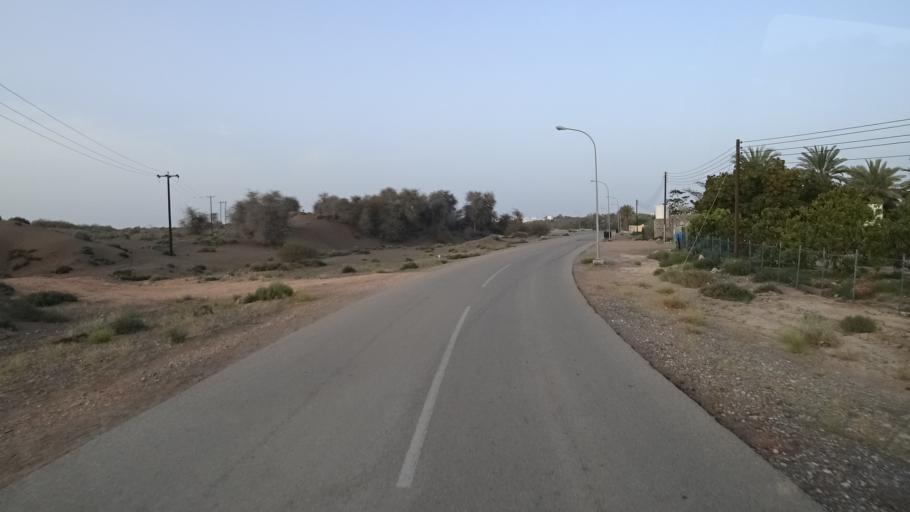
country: OM
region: Muhafazat Masqat
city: Muscat
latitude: 23.2083
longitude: 58.9709
